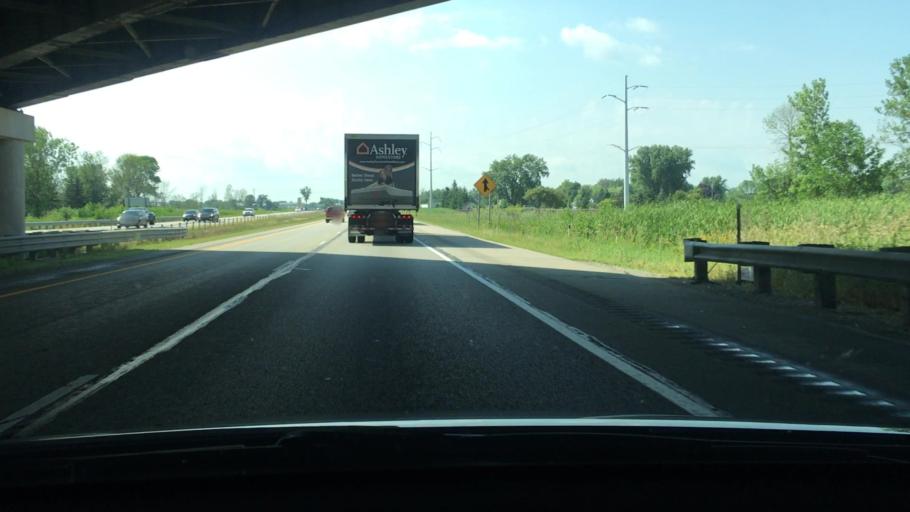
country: US
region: Wisconsin
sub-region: Fond du Lac County
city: North Fond du Lac
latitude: 43.8067
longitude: -88.4996
